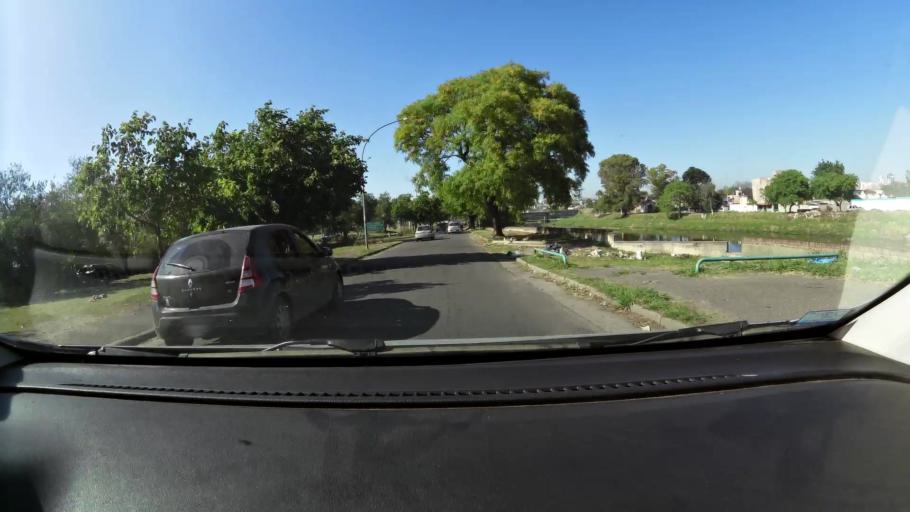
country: AR
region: Cordoba
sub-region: Departamento de Capital
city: Cordoba
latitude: -31.4184
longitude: -64.1573
